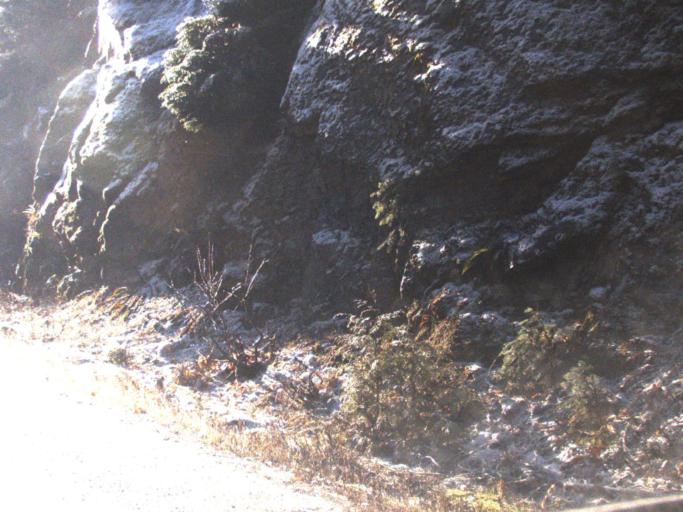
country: US
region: Washington
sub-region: Snohomish County
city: Darrington
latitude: 48.7034
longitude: -121.1117
